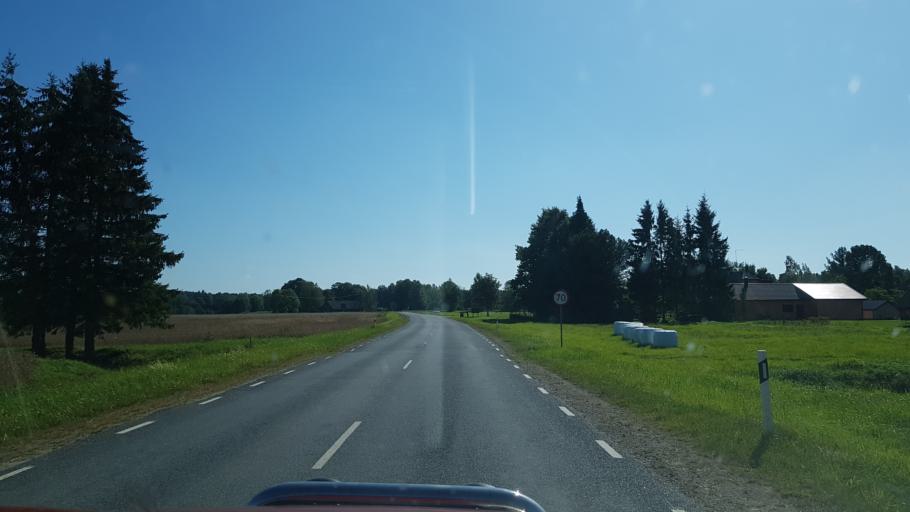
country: EE
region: Polvamaa
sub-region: Polva linn
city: Polva
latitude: 58.2717
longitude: 27.1226
